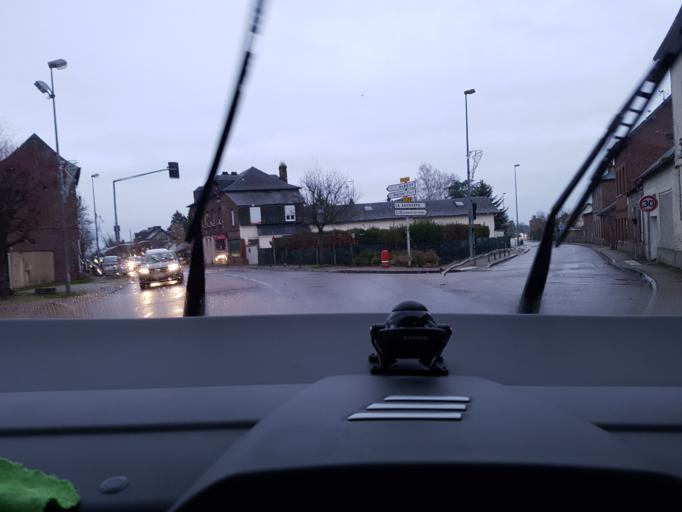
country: FR
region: Haute-Normandie
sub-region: Departement de l'Eure
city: Saint-Pierre-des-Fleurs
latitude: 49.2504
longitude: 0.9662
